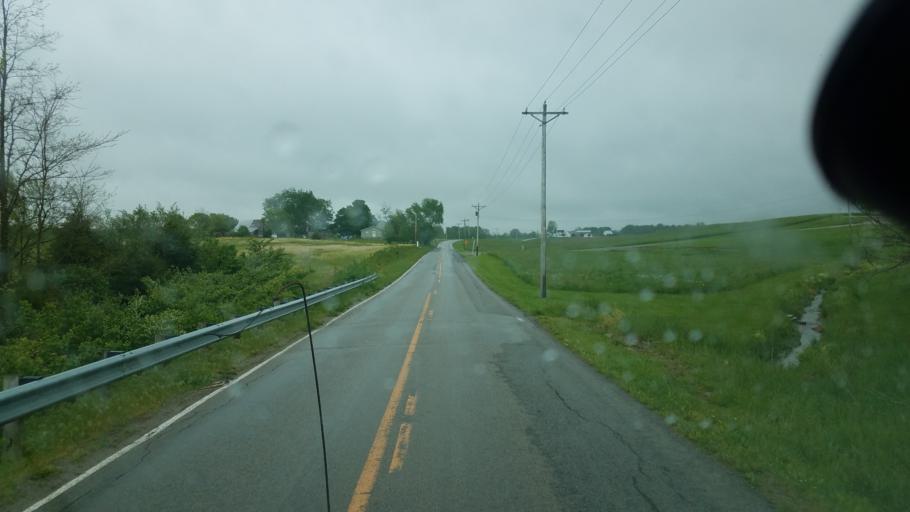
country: US
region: Ohio
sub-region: Highland County
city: Greenfield
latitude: 39.3381
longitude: -83.4531
